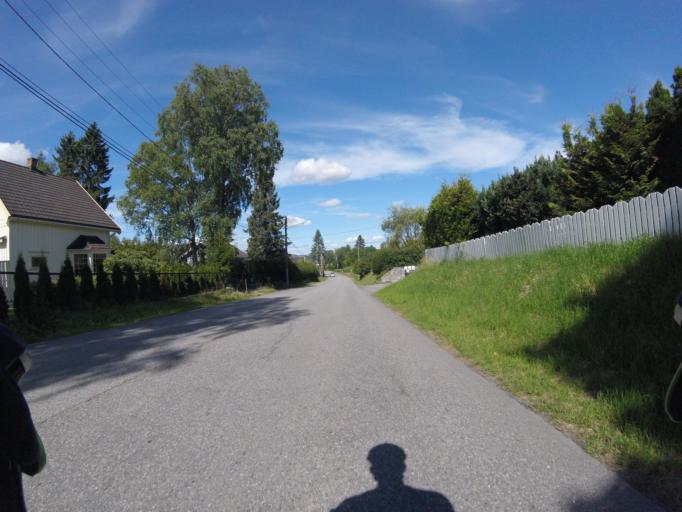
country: NO
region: Akershus
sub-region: Skedsmo
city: Lillestrom
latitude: 59.9480
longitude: 11.0207
